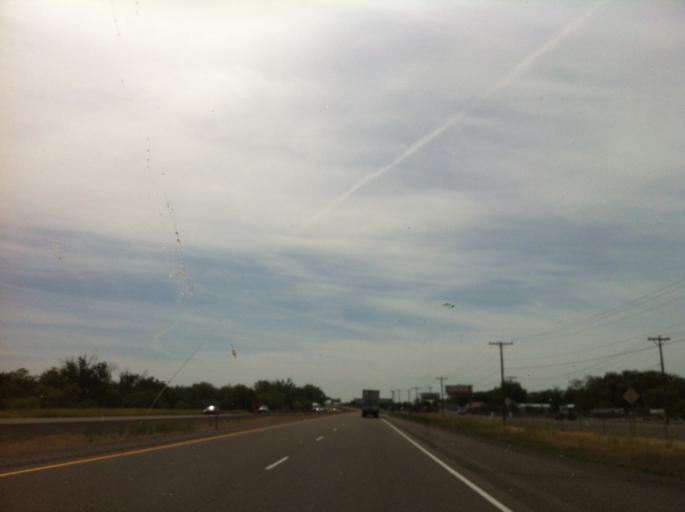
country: US
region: Oregon
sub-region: Malheur County
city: Ontario
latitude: 44.0448
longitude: -116.9718
